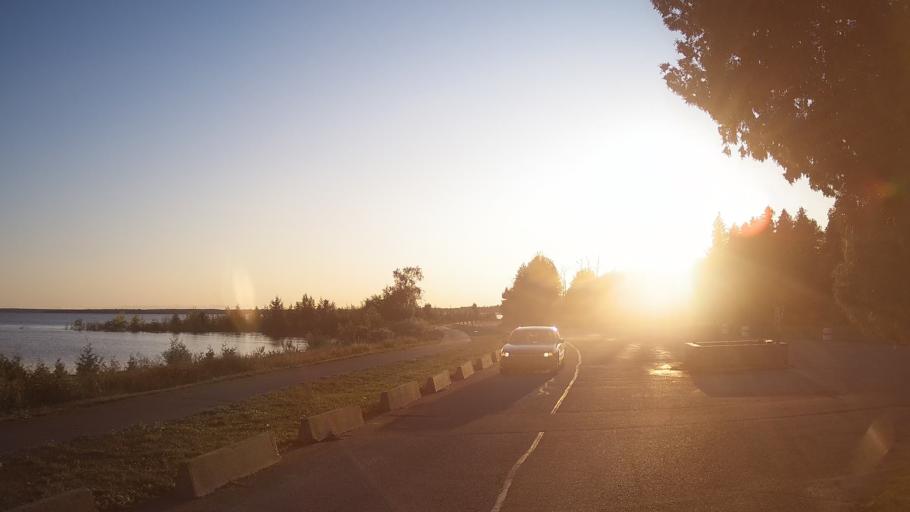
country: US
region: Michigan
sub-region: Schoolcraft County
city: Manistique
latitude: 45.9465
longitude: -86.2345
